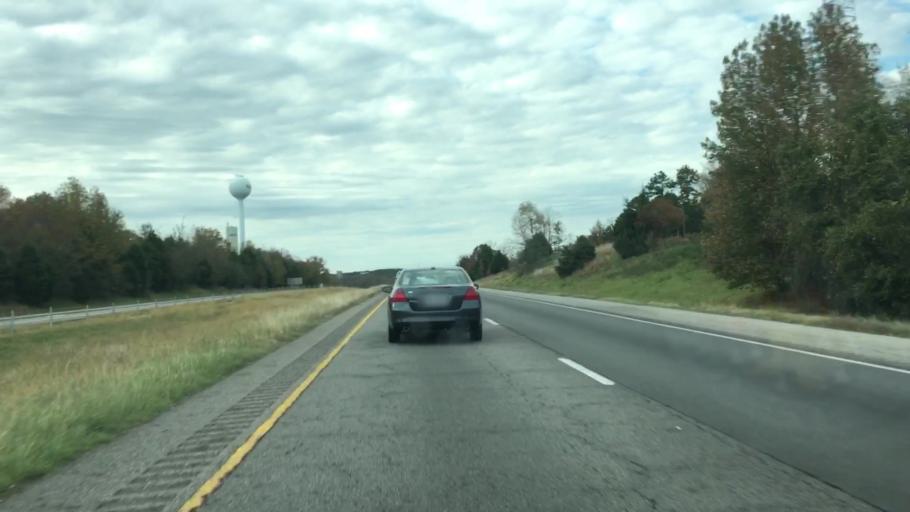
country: US
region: Arkansas
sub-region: Faulkner County
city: Conway
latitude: 35.1470
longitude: -92.5387
